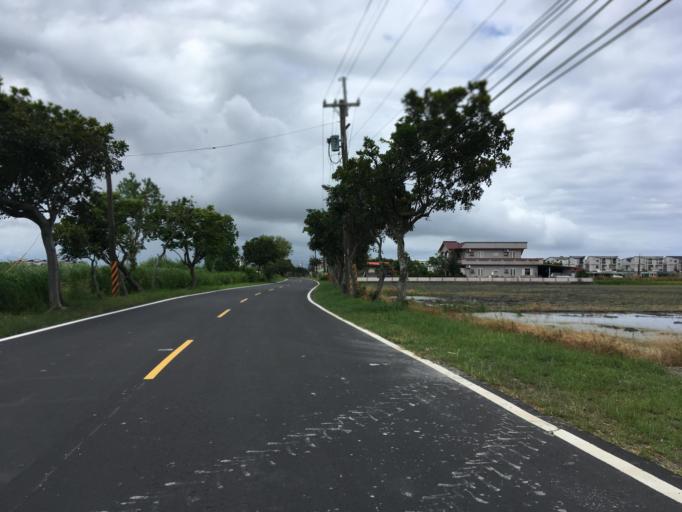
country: TW
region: Taiwan
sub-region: Yilan
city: Yilan
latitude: 24.6849
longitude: 121.8084
